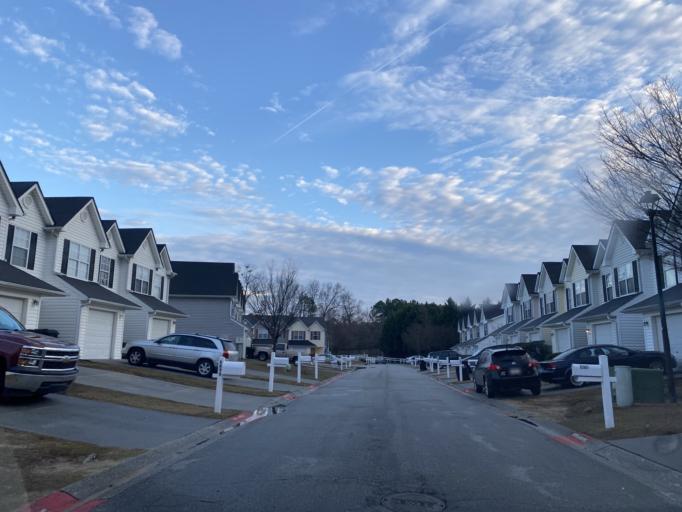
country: US
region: Georgia
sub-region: Cobb County
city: Mableton
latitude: 33.7851
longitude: -84.5497
